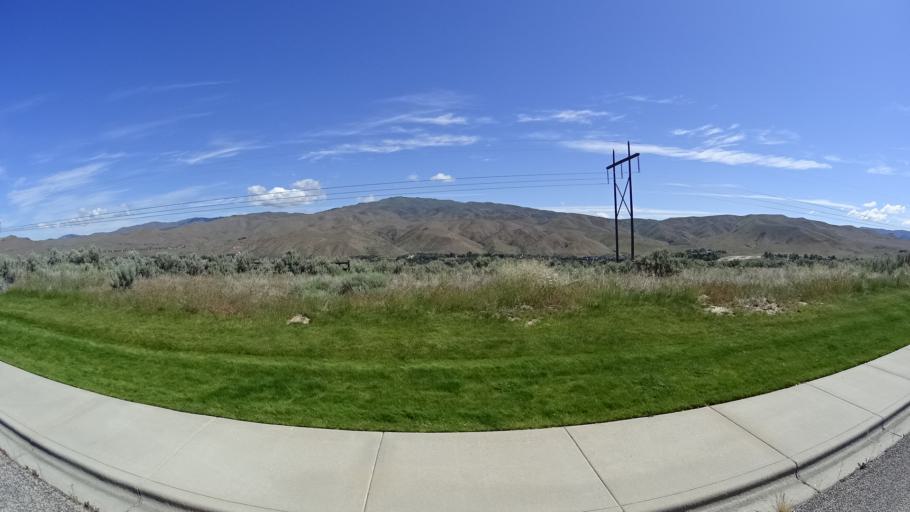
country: US
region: Idaho
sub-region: Ada County
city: Boise
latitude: 43.5473
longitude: -116.1168
